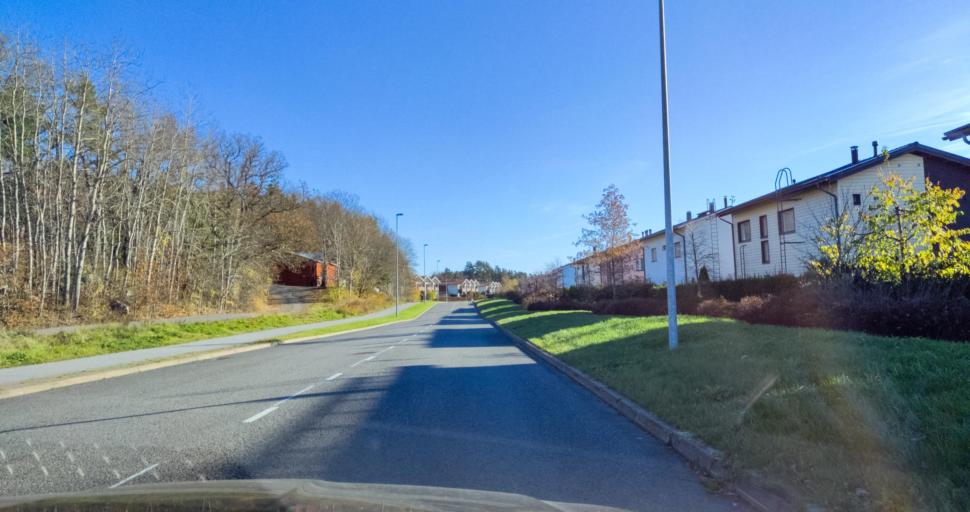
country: FI
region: Varsinais-Suomi
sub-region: Turku
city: Turku
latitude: 60.4109
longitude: 22.2110
